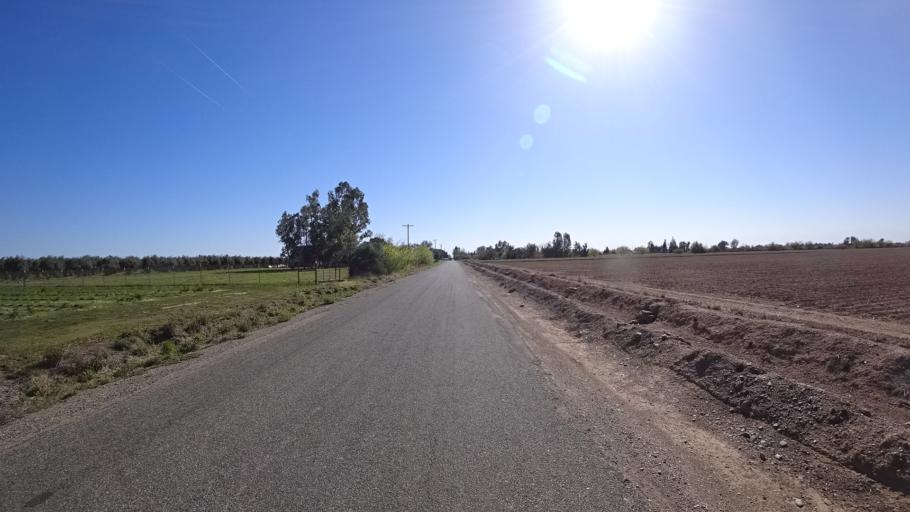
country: US
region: California
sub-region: Glenn County
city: Orland
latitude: 39.7369
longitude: -122.2326
